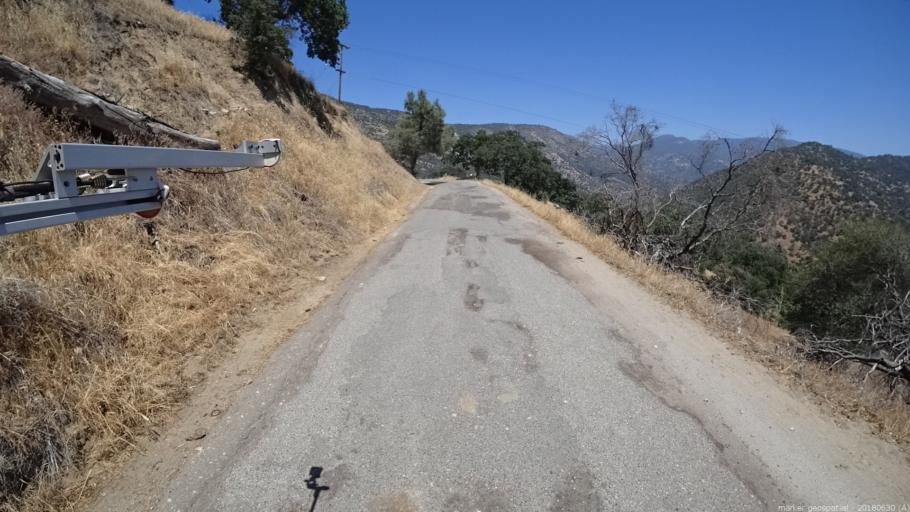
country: US
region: California
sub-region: Fresno County
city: Auberry
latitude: 37.1659
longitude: -119.4396
